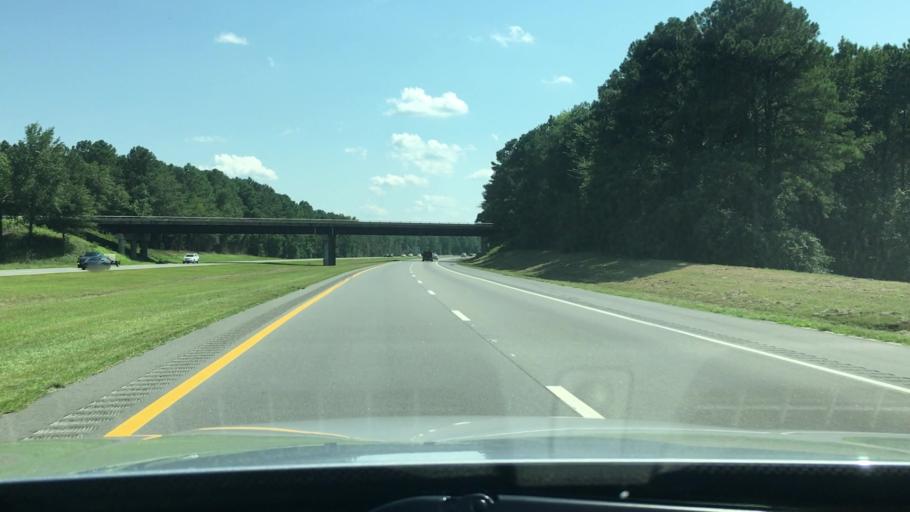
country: US
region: North Carolina
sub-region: Cumberland County
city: Vander
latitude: 35.0261
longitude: -78.8087
